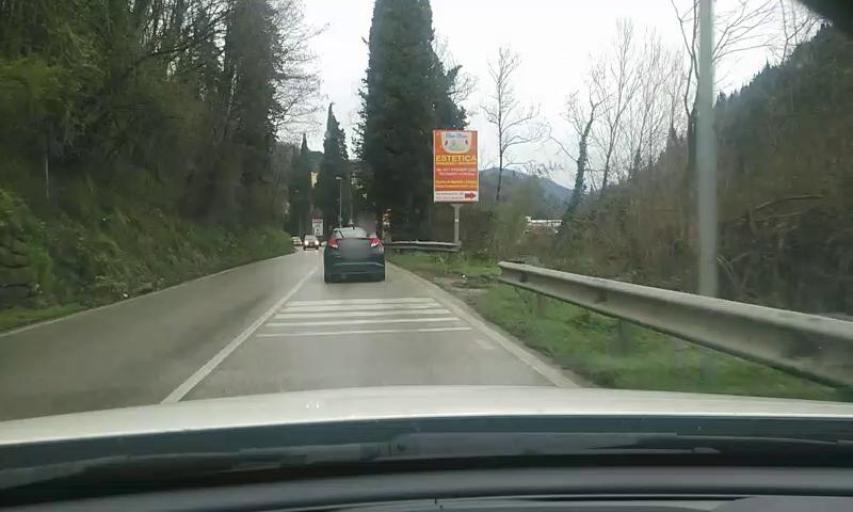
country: IT
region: Tuscany
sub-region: Provincia di Prato
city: Vaiano
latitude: 43.9431
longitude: 11.1255
